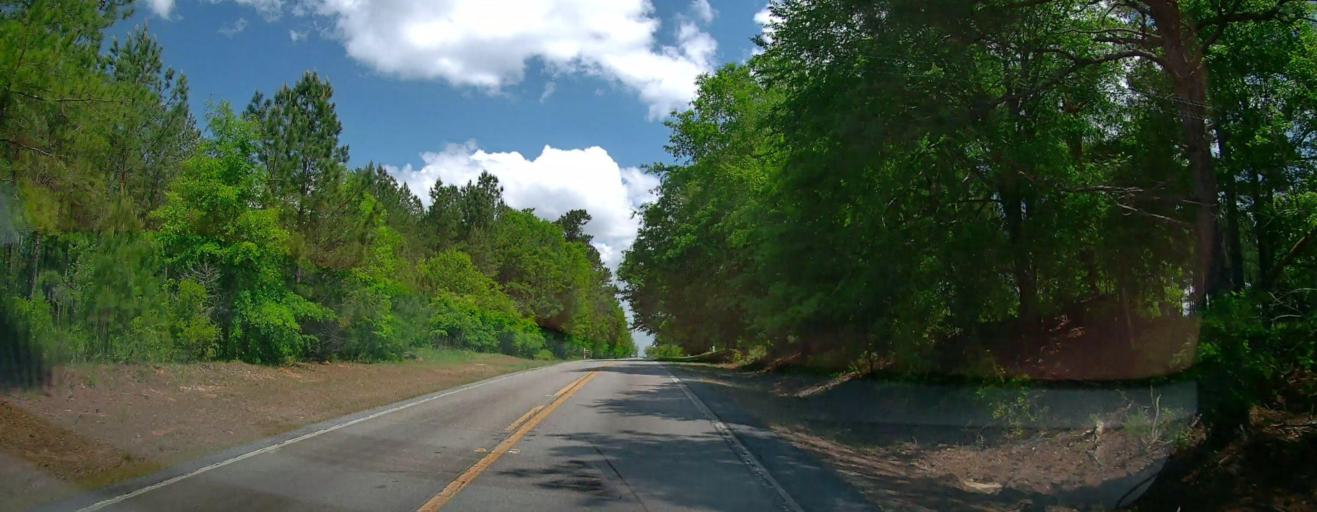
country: US
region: Georgia
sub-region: Bleckley County
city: Cochran
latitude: 32.4692
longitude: -83.2775
